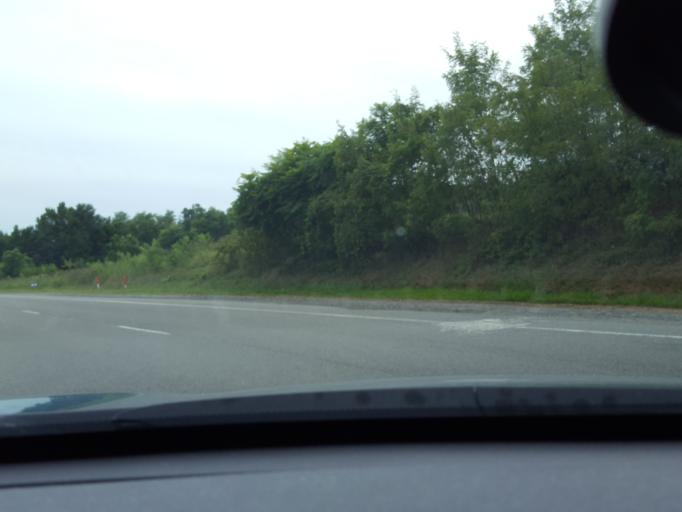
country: US
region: Virginia
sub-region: Caroline County
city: Bowling Green
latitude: 38.0428
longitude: -77.3444
